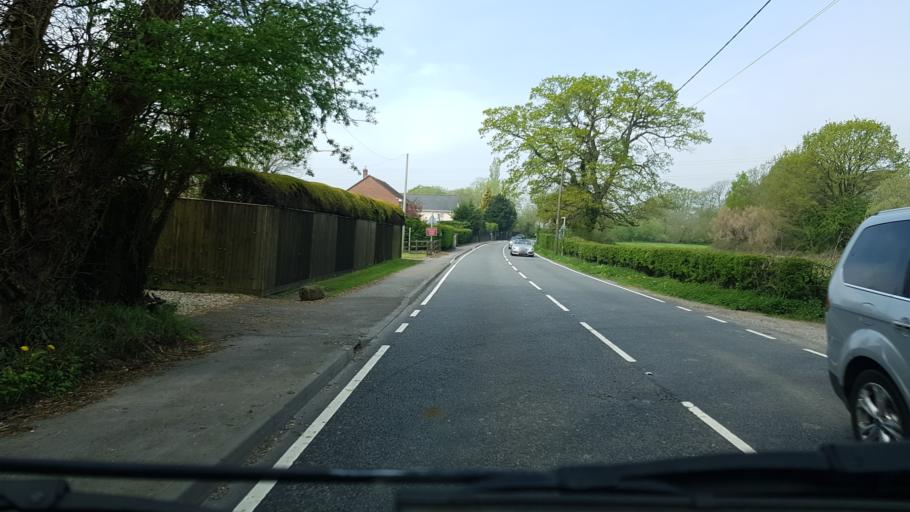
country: GB
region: England
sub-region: Hampshire
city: Kingsclere
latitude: 51.3306
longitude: -1.2521
